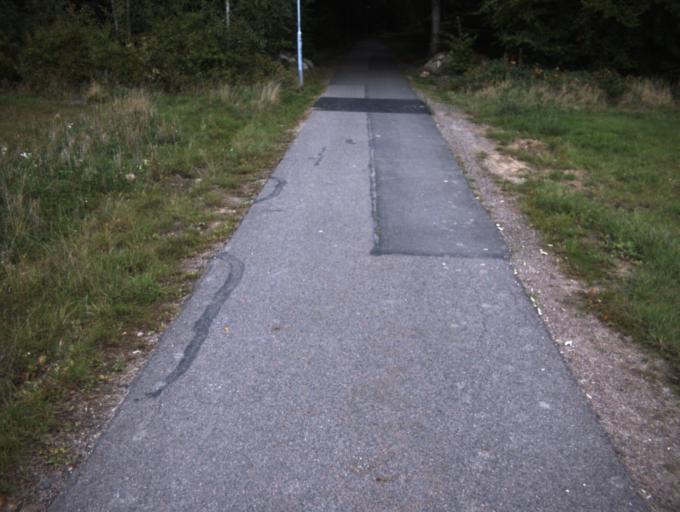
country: SE
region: Skane
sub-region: Helsingborg
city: Helsingborg
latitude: 56.0838
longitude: 12.6786
